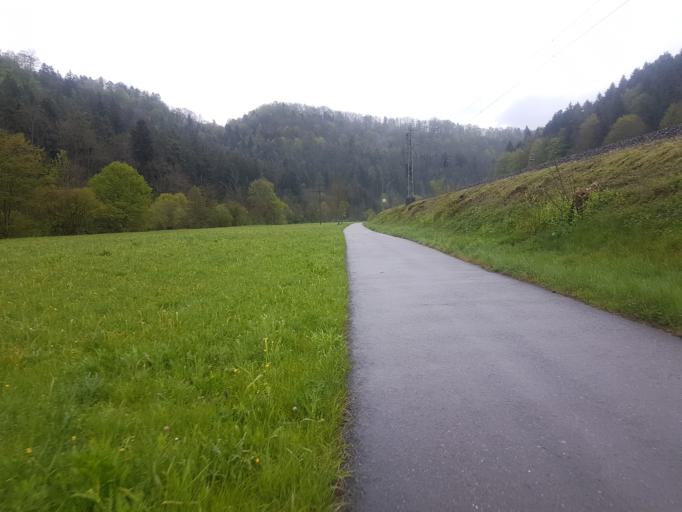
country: DE
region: Baden-Wuerttemberg
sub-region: Freiburg Region
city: Epfendorf
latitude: 48.2346
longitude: 8.6065
